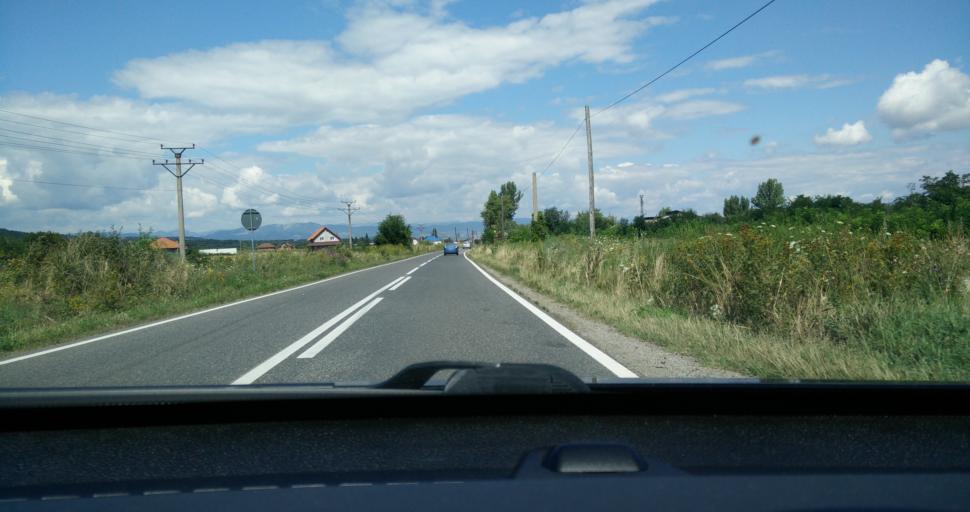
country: RO
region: Alba
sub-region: Comuna Sasciori
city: Sebesel
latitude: 45.9017
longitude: 23.5579
